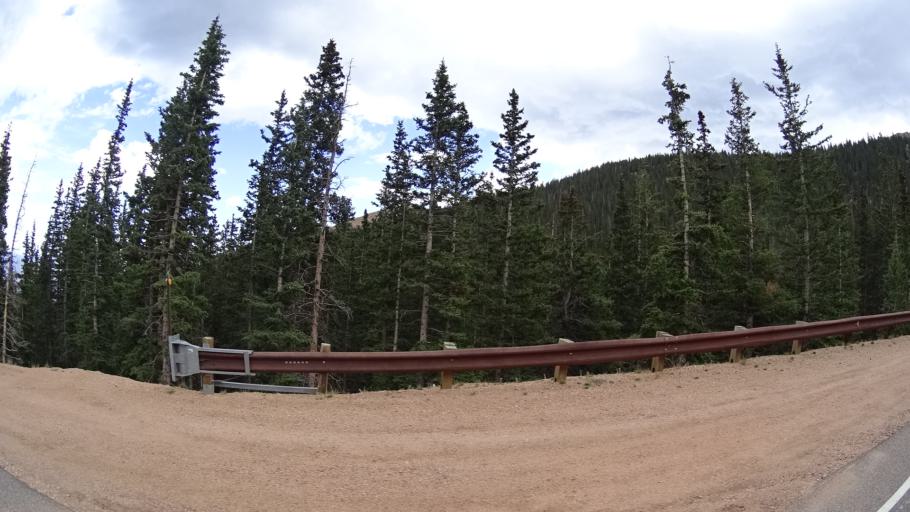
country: US
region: Colorado
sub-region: El Paso County
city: Cascade-Chipita Park
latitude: 38.8792
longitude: -105.0726
